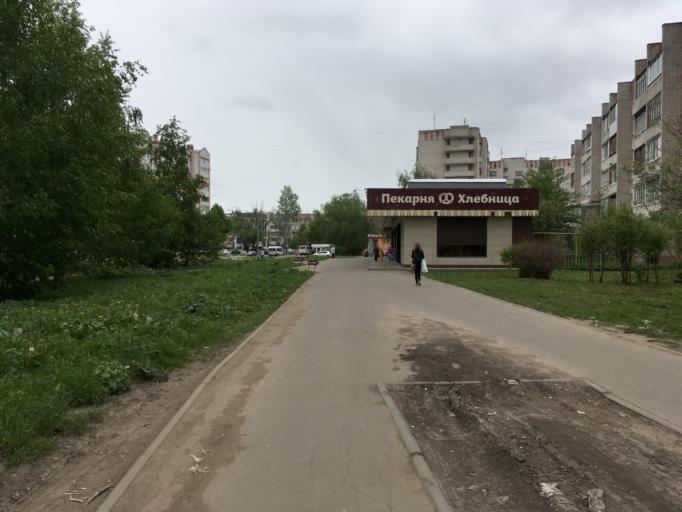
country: RU
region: Mariy-El
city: Yoshkar-Ola
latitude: 56.6456
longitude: 47.8613
